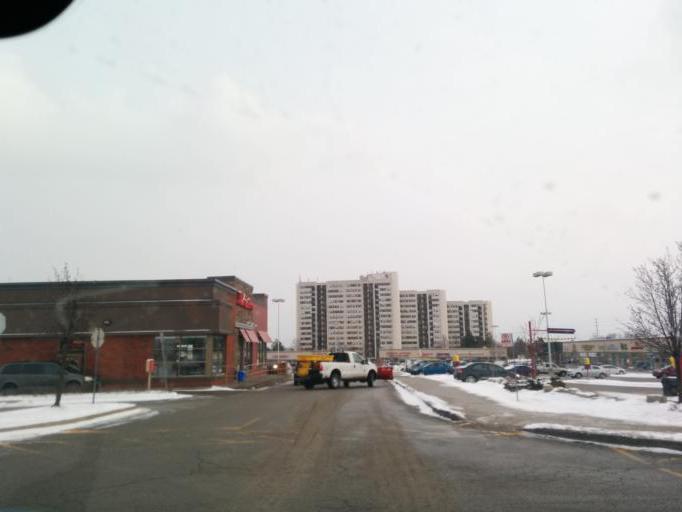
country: CA
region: Ontario
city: Mississauga
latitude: 43.5816
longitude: -79.7600
